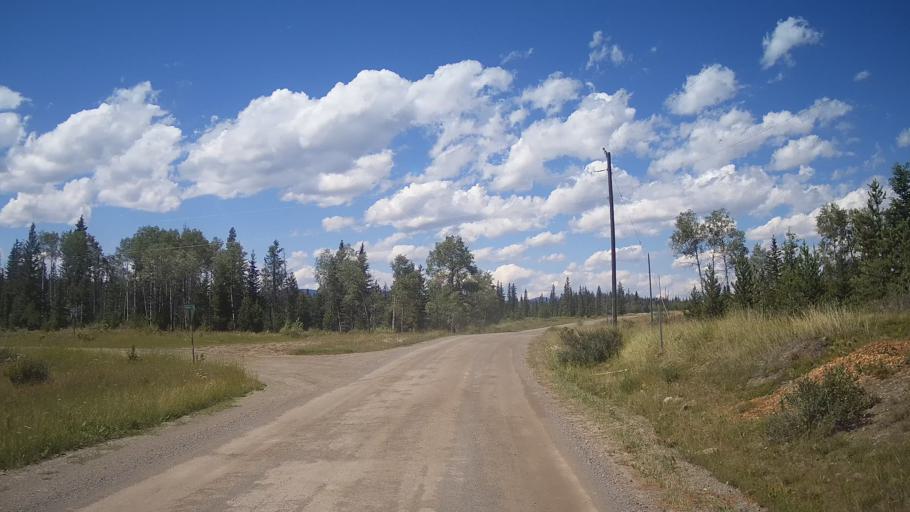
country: CA
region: British Columbia
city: Cache Creek
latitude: 51.2267
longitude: -121.6295
